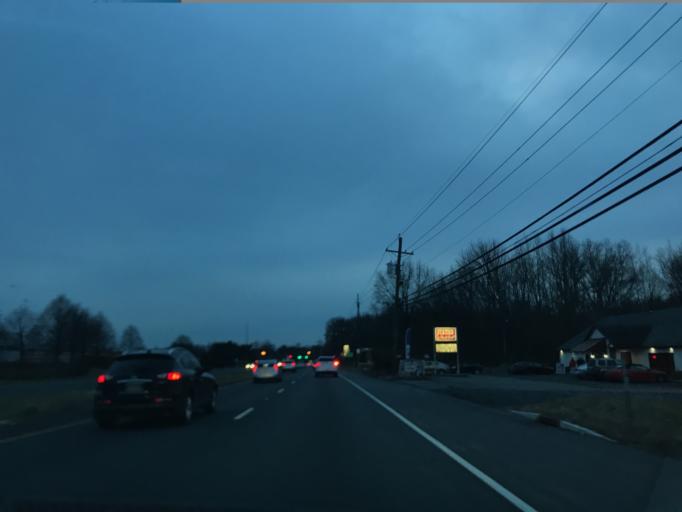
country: US
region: New Jersey
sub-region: Middlesex County
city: Cranbury
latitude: 40.3321
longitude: -74.5052
